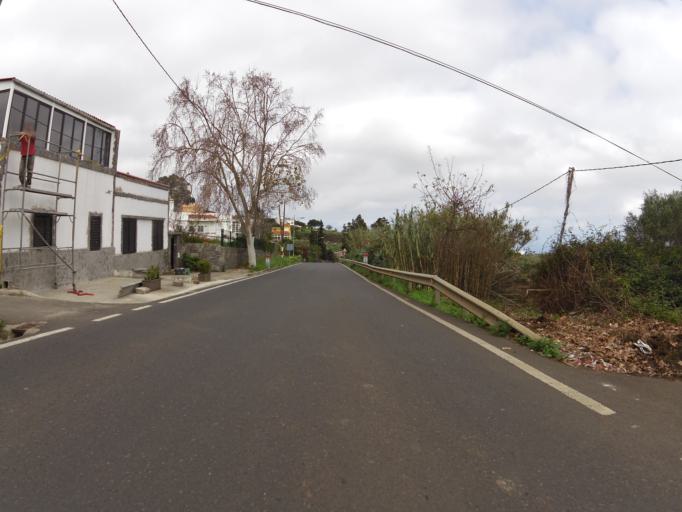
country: ES
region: Canary Islands
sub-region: Provincia de Las Palmas
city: Firgas
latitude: 28.0956
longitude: -15.5375
